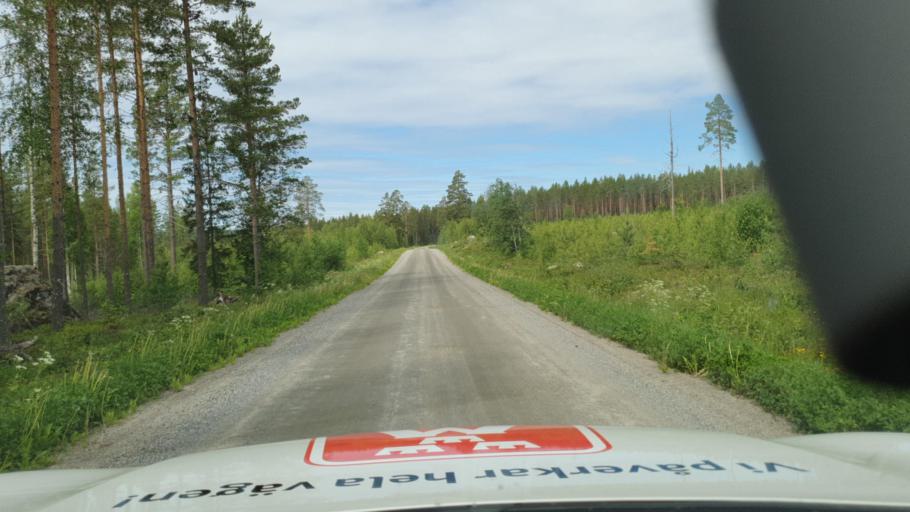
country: SE
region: Vaesterbotten
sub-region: Skelleftea Kommun
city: Burtraesk
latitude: 64.6161
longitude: 20.5805
